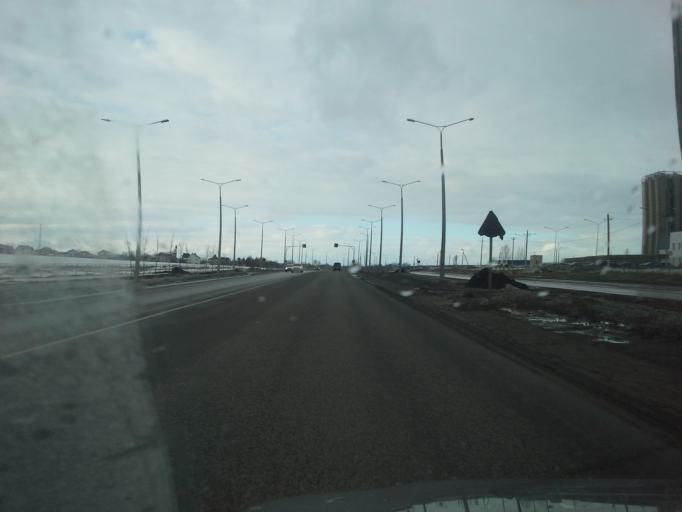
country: RU
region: Moskovskaya
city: Troitsk
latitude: 55.5103
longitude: 37.2469
